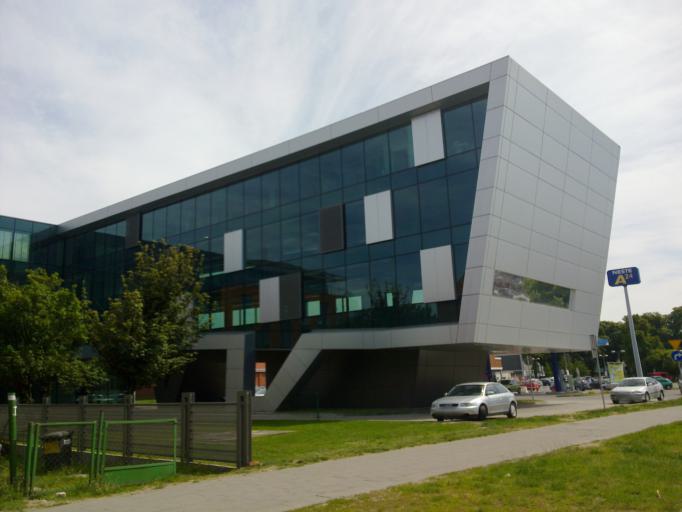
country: PL
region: Pomeranian Voivodeship
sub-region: Gdansk
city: Gdansk
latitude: 54.3842
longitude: 18.5956
